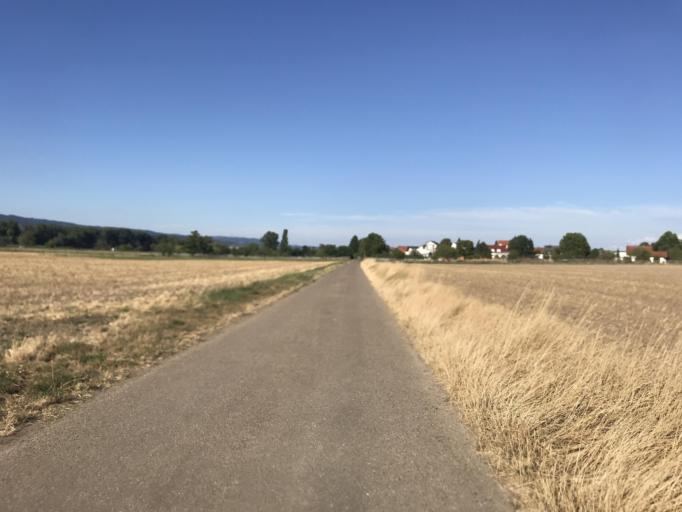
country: DE
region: Rheinland-Pfalz
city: Gau-Algesheim
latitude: 49.9744
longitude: 8.0032
